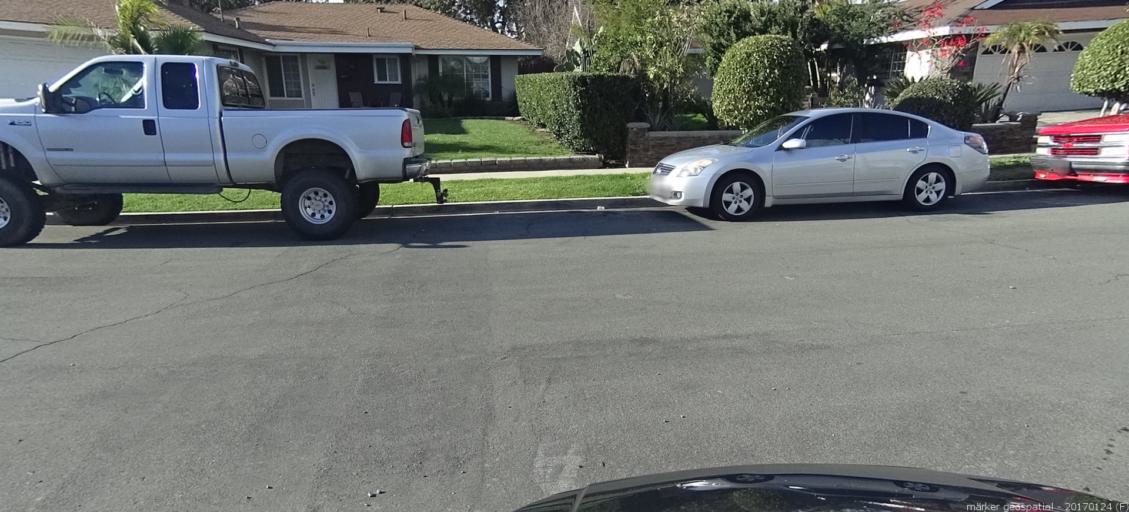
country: US
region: California
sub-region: Orange County
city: Laguna Hills
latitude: 33.6266
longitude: -117.6997
